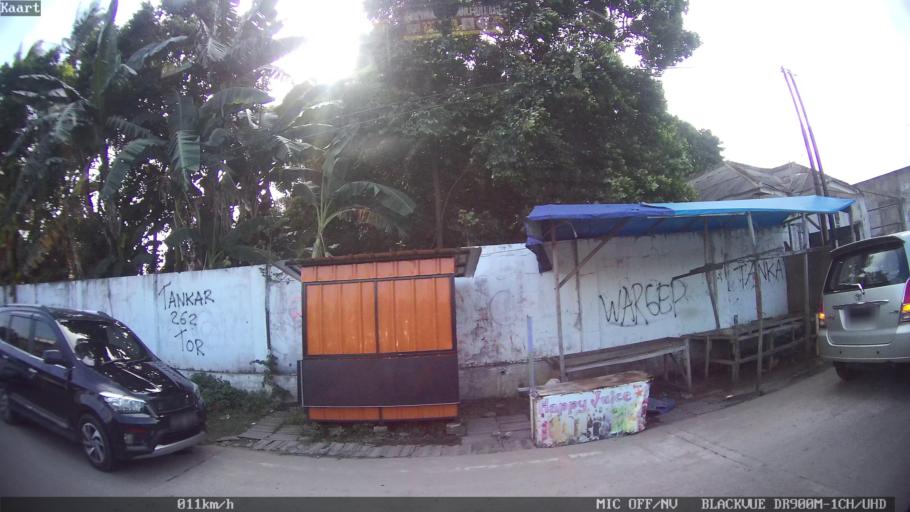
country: ID
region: Lampung
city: Kedaton
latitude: -5.3721
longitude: 105.2271
